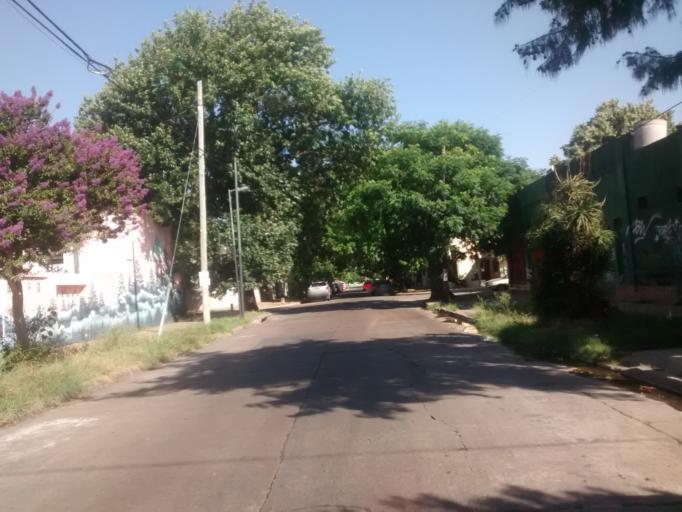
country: AR
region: Buenos Aires
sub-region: Partido de La Plata
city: La Plata
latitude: -34.9327
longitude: -57.9326
